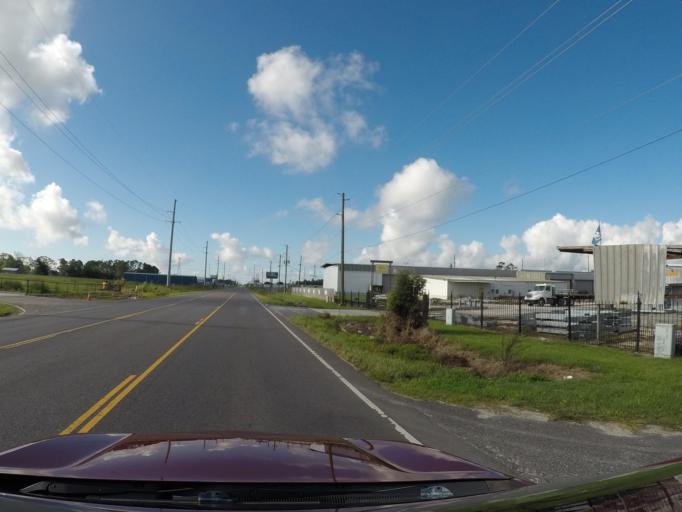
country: US
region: Louisiana
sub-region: Calcasieu Parish
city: Carlyss
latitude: 30.2005
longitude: -93.3762
